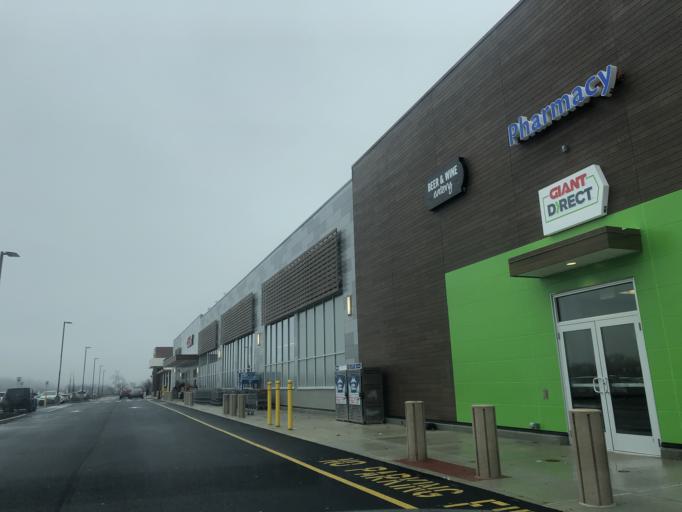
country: US
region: Pennsylvania
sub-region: Delaware County
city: Broomall
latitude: 39.9771
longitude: -75.3450
